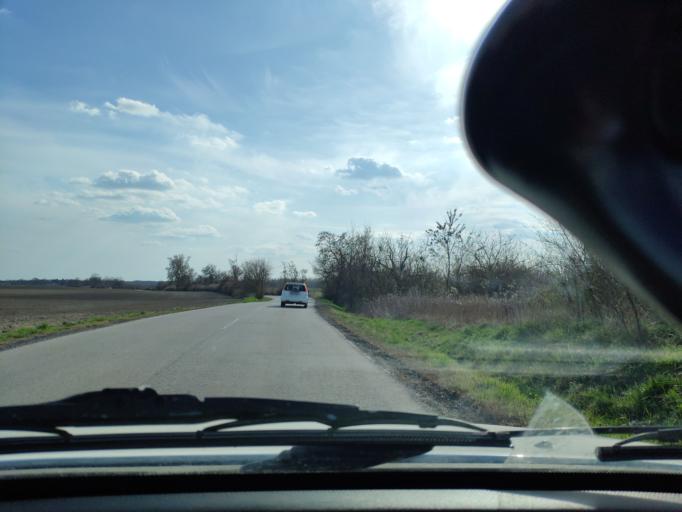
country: HU
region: Fejer
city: Adony
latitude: 47.1319
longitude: 18.8984
